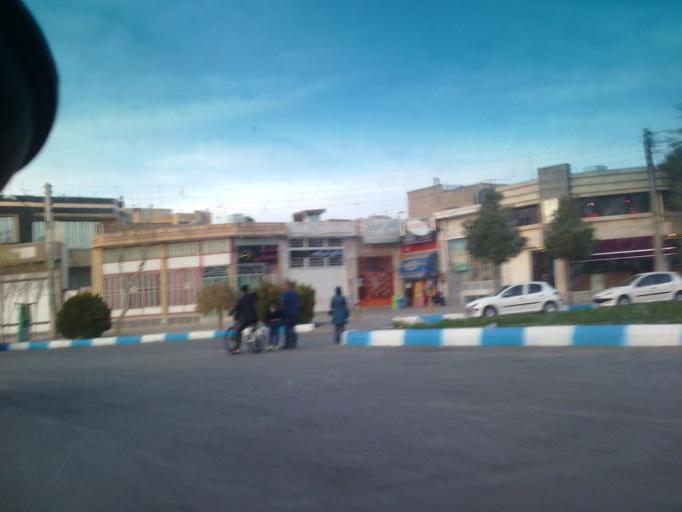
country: IR
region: Isfahan
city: Shahin Shahr
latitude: 32.8749
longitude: 51.5542
